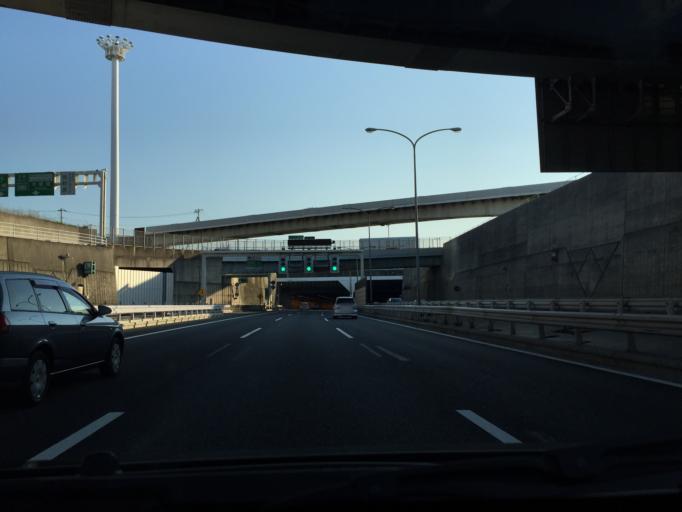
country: JP
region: Kanagawa
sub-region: Kawasaki-shi
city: Kawasaki
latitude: 35.5146
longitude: 139.7888
